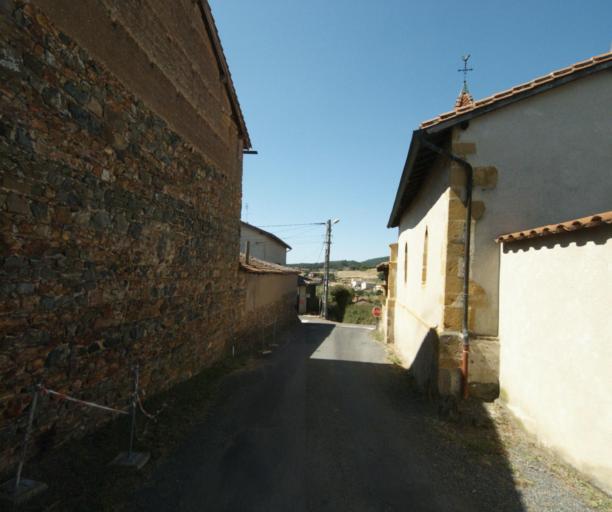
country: FR
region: Rhone-Alpes
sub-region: Departement du Rhone
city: Bessenay
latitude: 45.7998
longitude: 4.5489
